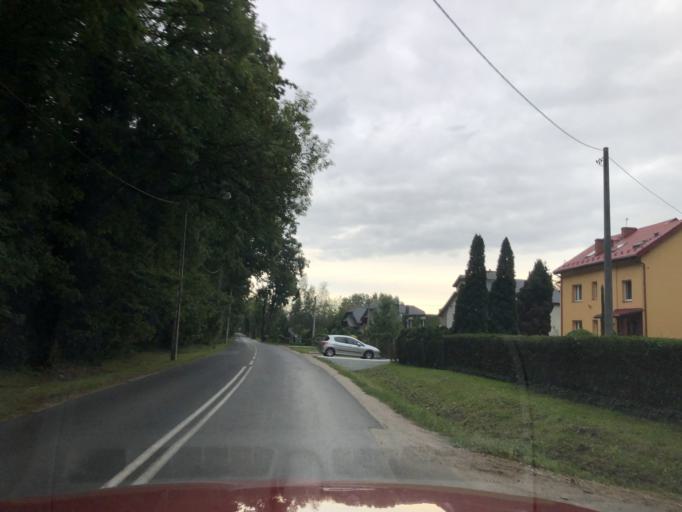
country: PL
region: Lower Silesian Voivodeship
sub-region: Powiat wroclawski
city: Dlugoleka
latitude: 51.1915
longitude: 17.1839
